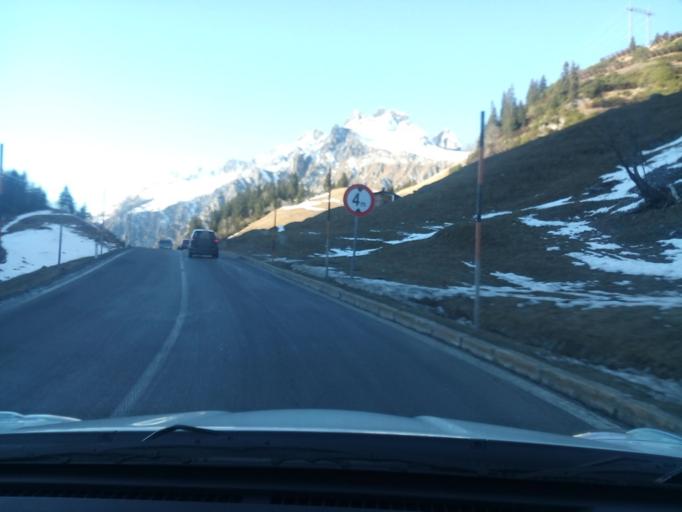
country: AT
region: Vorarlberg
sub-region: Politischer Bezirk Bludenz
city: Lech
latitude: 47.1386
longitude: 10.1756
